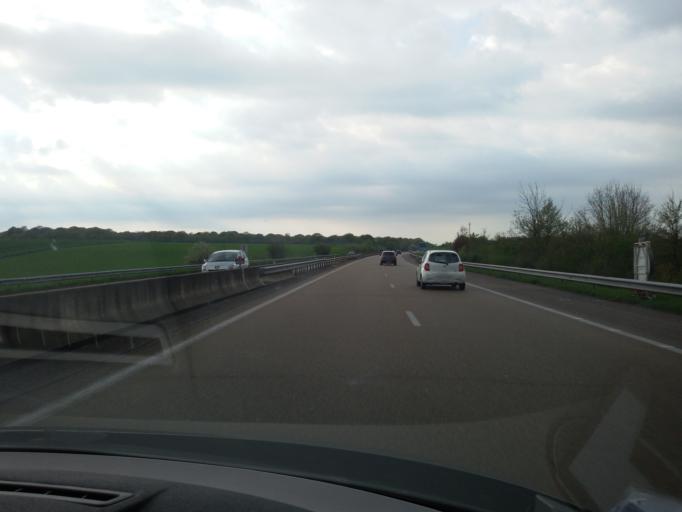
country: FR
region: Champagne-Ardenne
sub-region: Departement de la Haute-Marne
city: Chamarandes-Choignes
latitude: 47.9559
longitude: 5.1578
